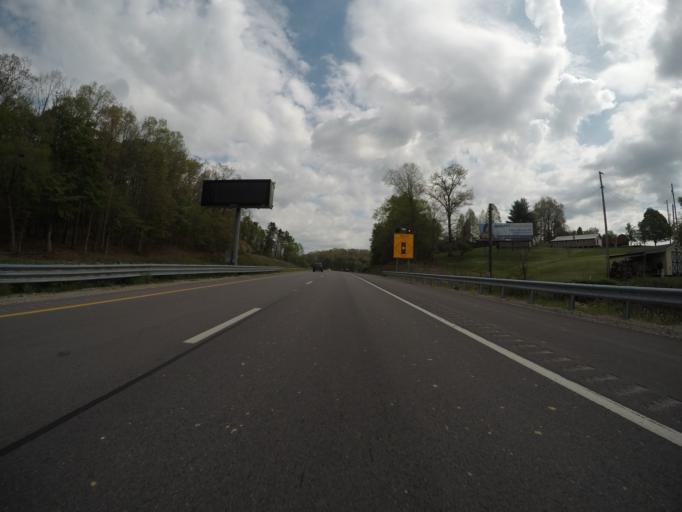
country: US
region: West Virginia
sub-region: Kanawha County
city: Alum Creek
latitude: 38.2735
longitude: -81.7828
